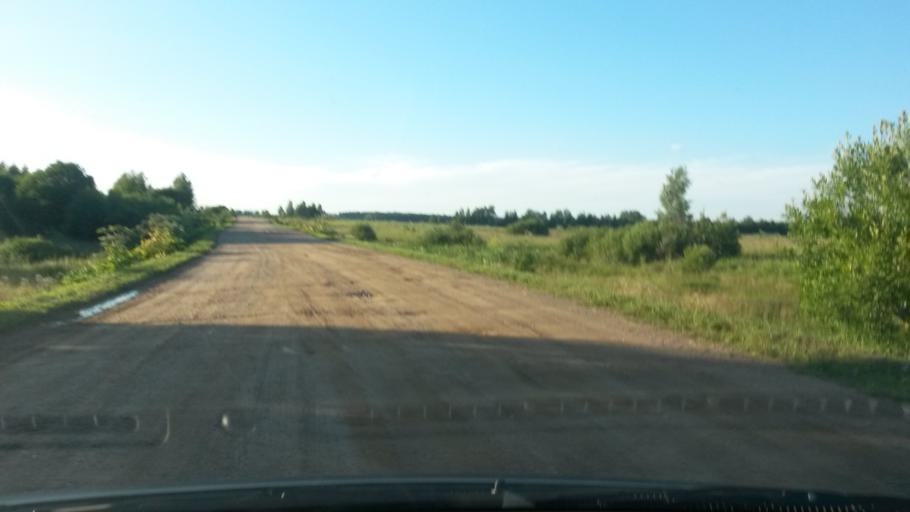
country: RU
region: Jaroslavl
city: Dubki
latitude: 57.2593
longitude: 40.1535
